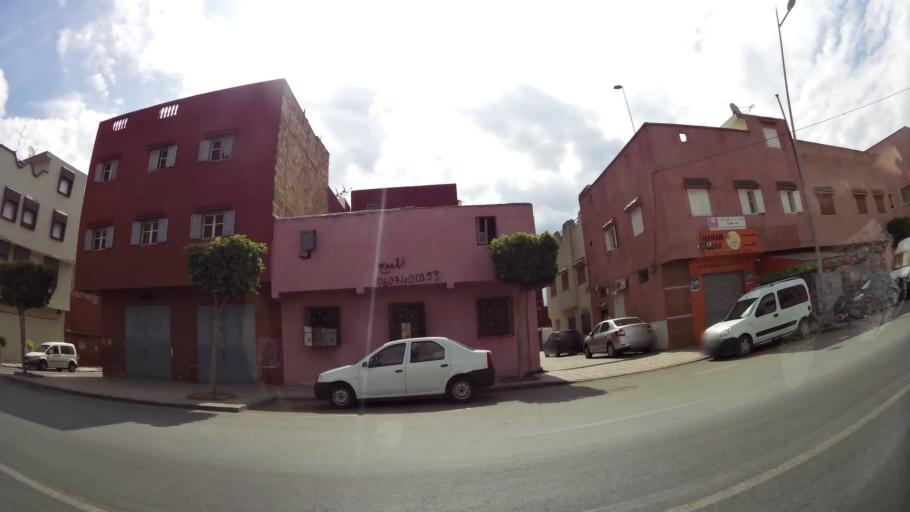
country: MA
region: Gharb-Chrarda-Beni Hssen
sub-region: Kenitra Province
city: Kenitra
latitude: 34.2584
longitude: -6.5604
